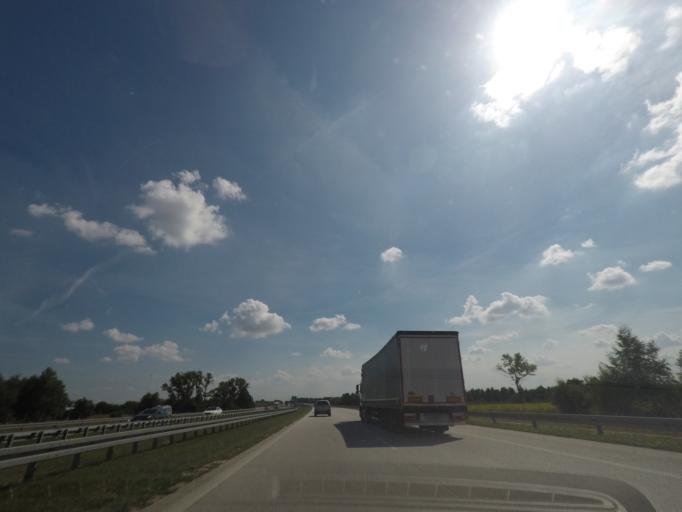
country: PL
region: Lodz Voivodeship
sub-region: Powiat lodzki wschodni
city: Andrespol
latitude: 51.7611
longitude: 19.5956
